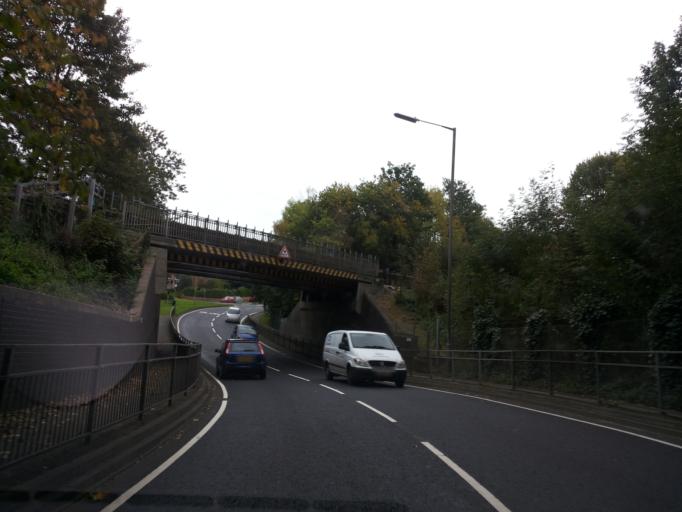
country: GB
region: England
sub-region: Buckinghamshire
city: Little Chalfont
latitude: 51.6677
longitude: -0.5601
